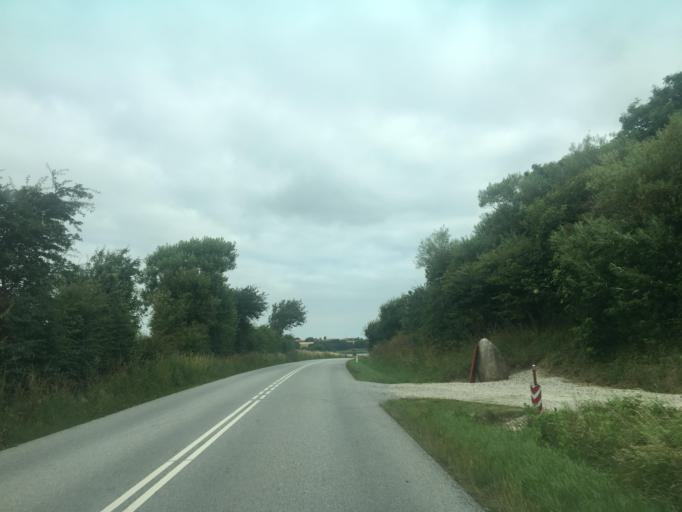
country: DK
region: North Denmark
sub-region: Thisted Kommune
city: Thisted
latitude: 56.8678
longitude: 8.6200
